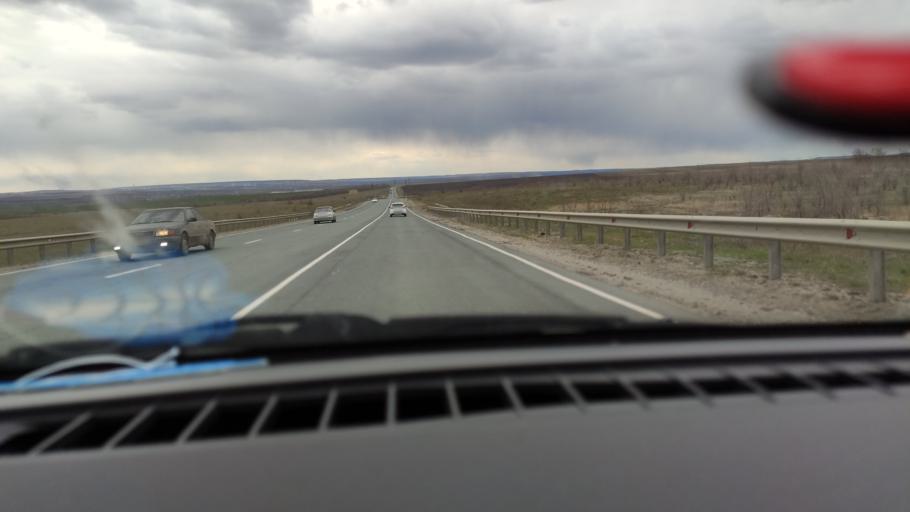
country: RU
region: Saratov
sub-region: Saratovskiy Rayon
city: Saratov
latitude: 51.7598
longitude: 46.0707
